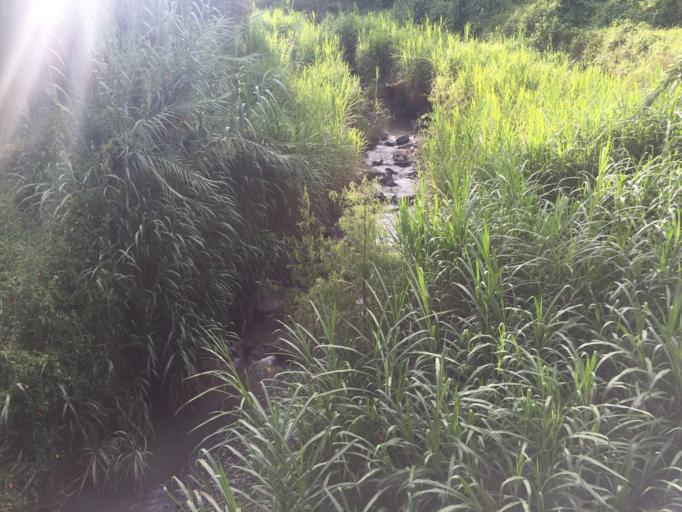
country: CO
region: Cundinamarca
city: Tenza
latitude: 5.0949
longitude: -73.4445
